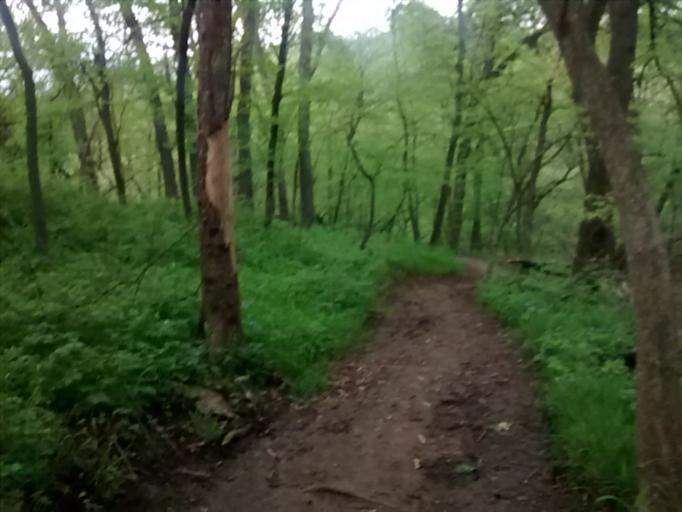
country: US
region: Nebraska
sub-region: Sarpy County
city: Bellevue
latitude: 41.1796
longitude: -95.9136
